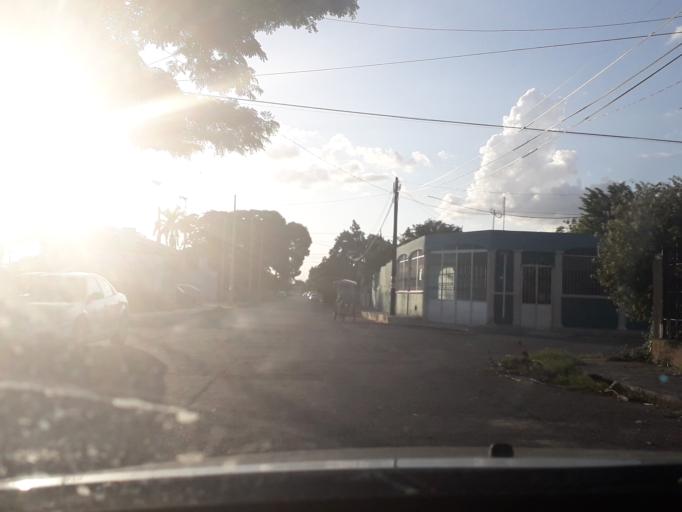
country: MX
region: Yucatan
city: Merida
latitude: 20.9775
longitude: -89.6504
